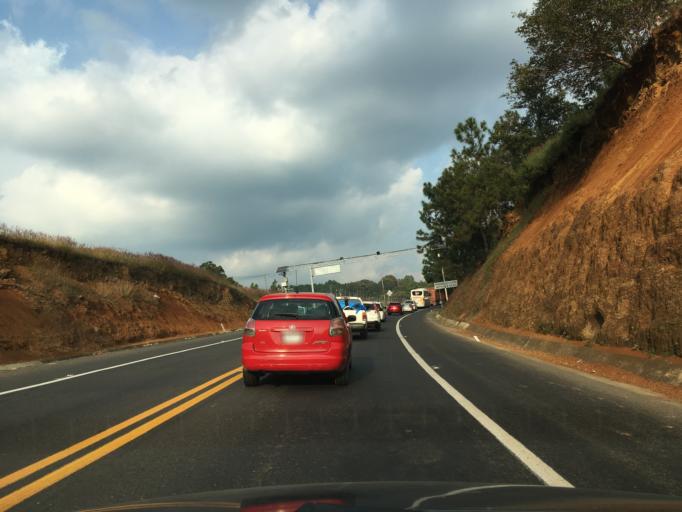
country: MX
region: Michoacan
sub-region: Ziracuaretiro
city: Patuan
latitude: 19.4399
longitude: -101.8867
